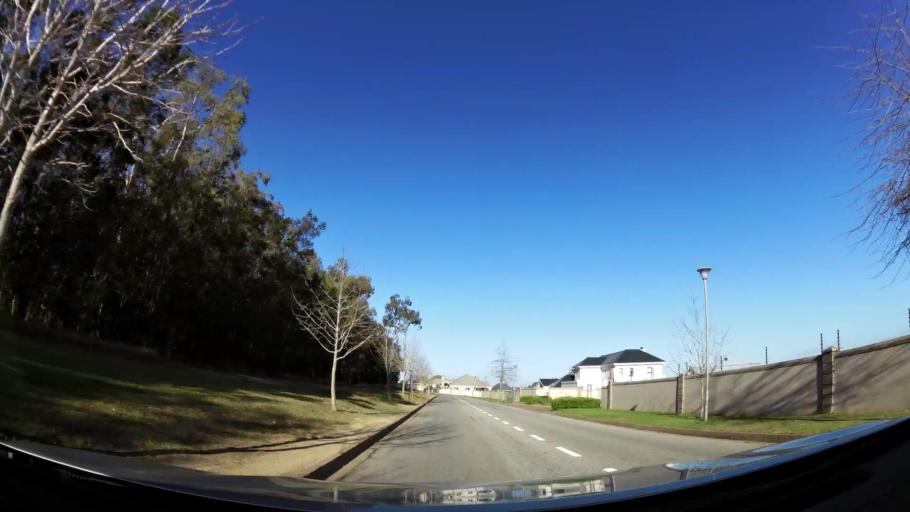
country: ZA
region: Western Cape
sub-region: Eden District Municipality
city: George
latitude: -33.9644
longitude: 22.4390
